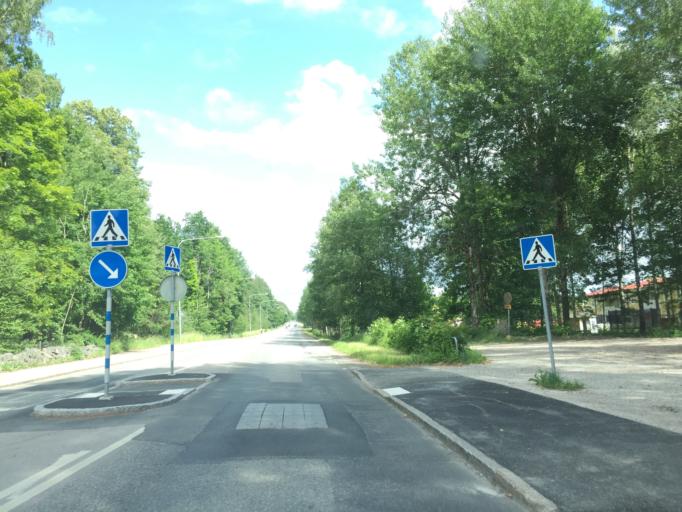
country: SE
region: OErebro
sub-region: Orebro Kommun
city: Orebro
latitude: 59.2417
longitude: 15.1823
